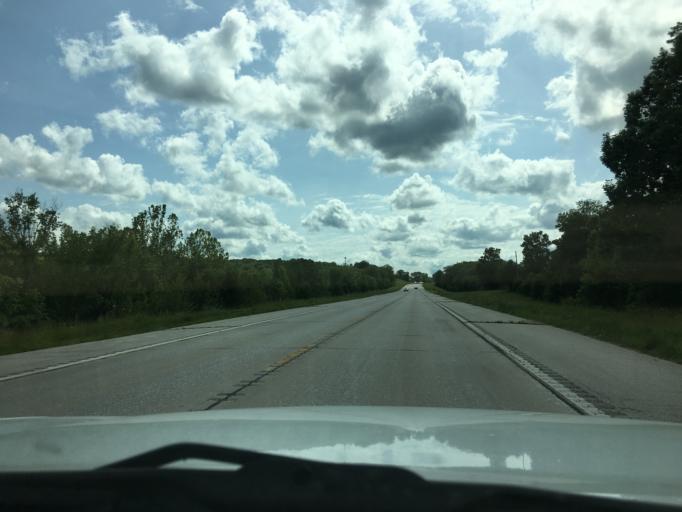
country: US
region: Missouri
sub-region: Franklin County
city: Gerald
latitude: 38.4144
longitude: -91.3036
